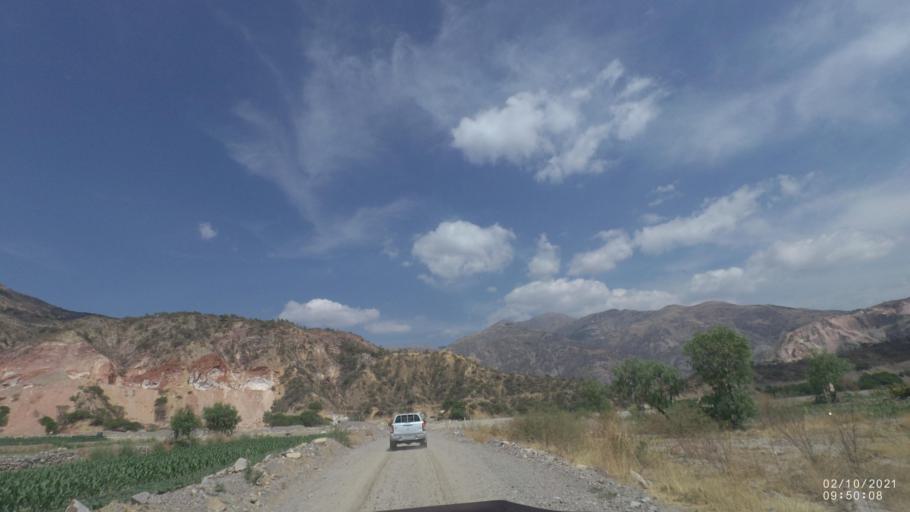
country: BO
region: Cochabamba
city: Irpa Irpa
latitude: -17.8011
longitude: -66.3368
